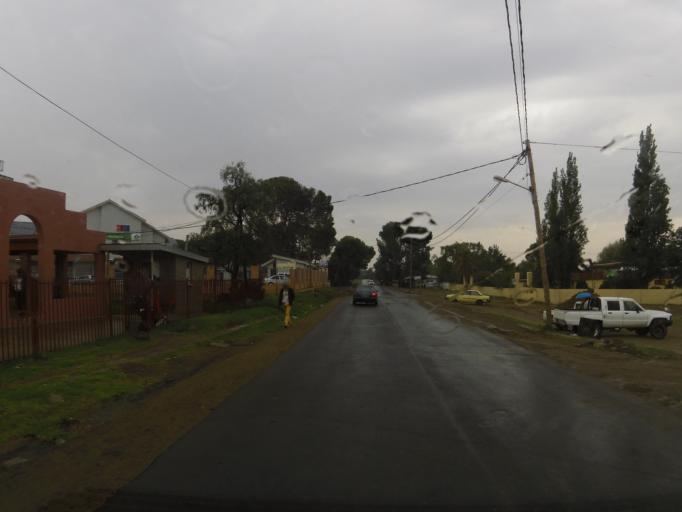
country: LS
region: Mafeteng
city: Mafeteng
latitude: -29.8213
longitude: 27.2405
